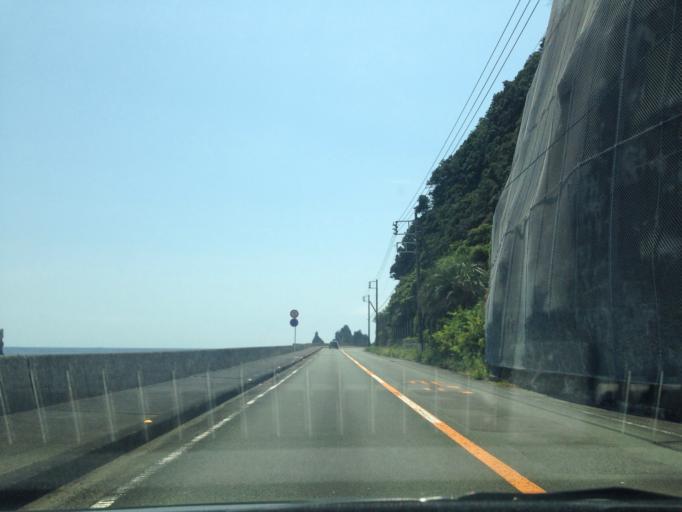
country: JP
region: Shizuoka
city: Shimoda
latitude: 34.6178
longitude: 138.8645
